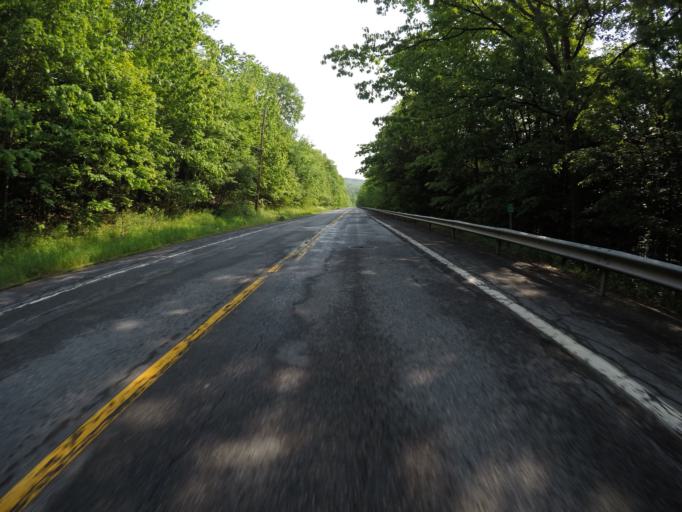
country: US
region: New York
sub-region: Sullivan County
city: Livingston Manor
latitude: 42.1218
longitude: -74.7261
